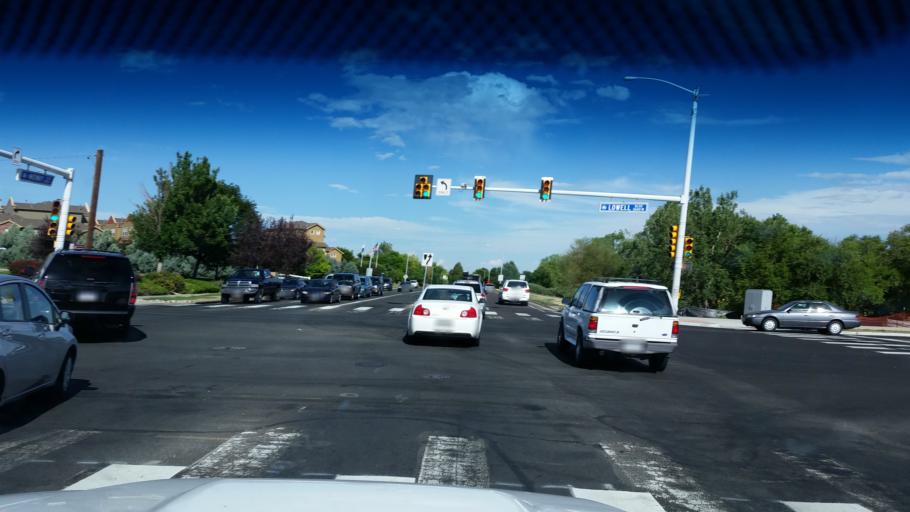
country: US
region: Colorado
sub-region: Broomfield County
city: Broomfield
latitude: 39.9287
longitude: -105.0347
